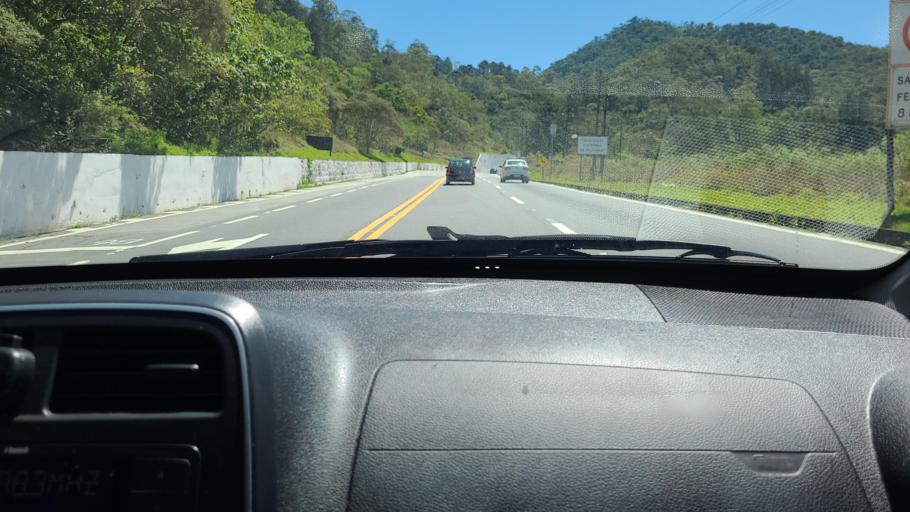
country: BR
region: Sao Paulo
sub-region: Campos Do Jordao
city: Campos do Jordao
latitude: -22.8301
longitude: -45.6248
